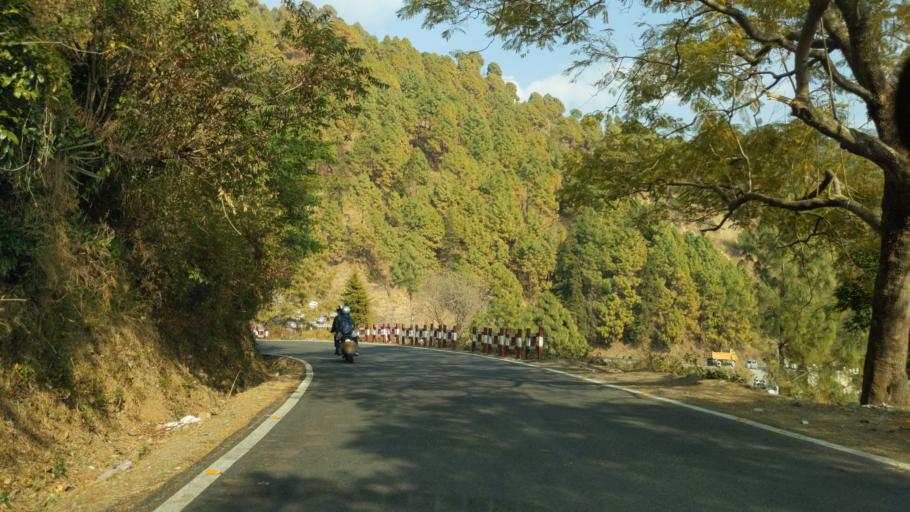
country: IN
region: Uttarakhand
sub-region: Naini Tal
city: Bhowali
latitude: 29.3776
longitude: 79.5297
